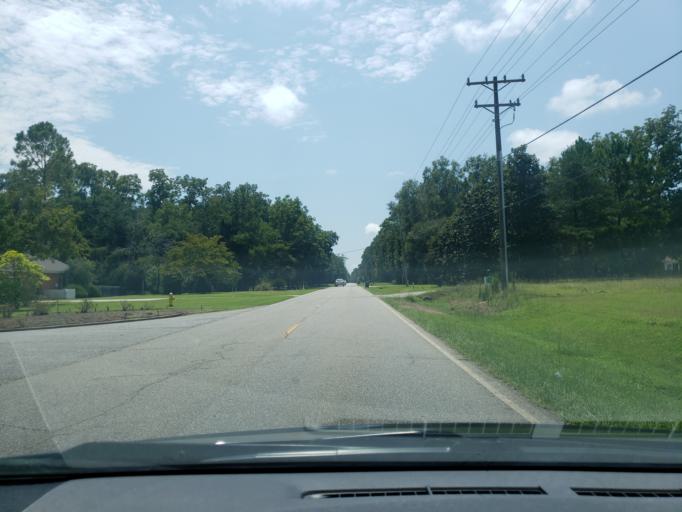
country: US
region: Georgia
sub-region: Dougherty County
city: Albany
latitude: 31.6032
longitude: -84.2769
